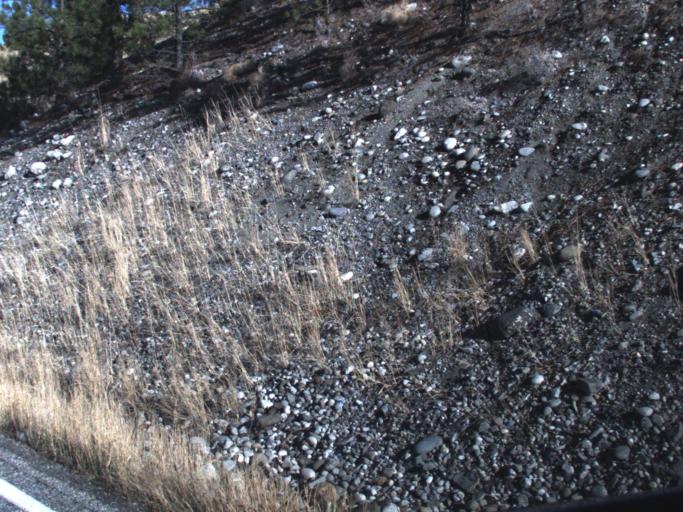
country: CA
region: British Columbia
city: Grand Forks
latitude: 48.8693
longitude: -118.6072
